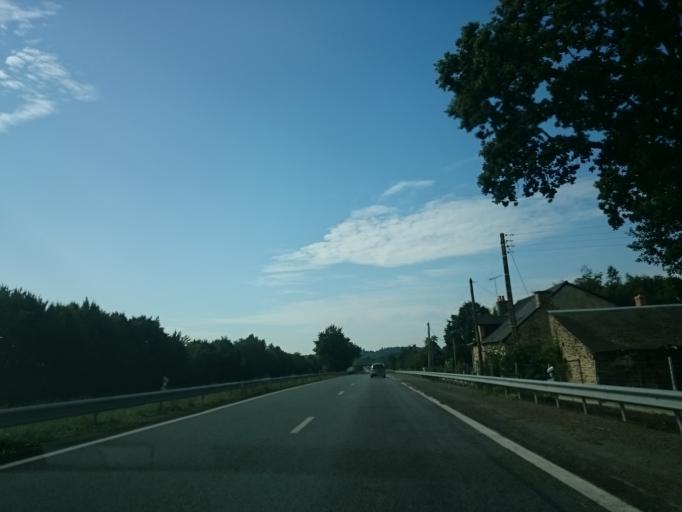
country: FR
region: Brittany
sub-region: Departement d'Ille-et-Vilaine
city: Bain-de-Bretagne
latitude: 47.8124
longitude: -1.6900
